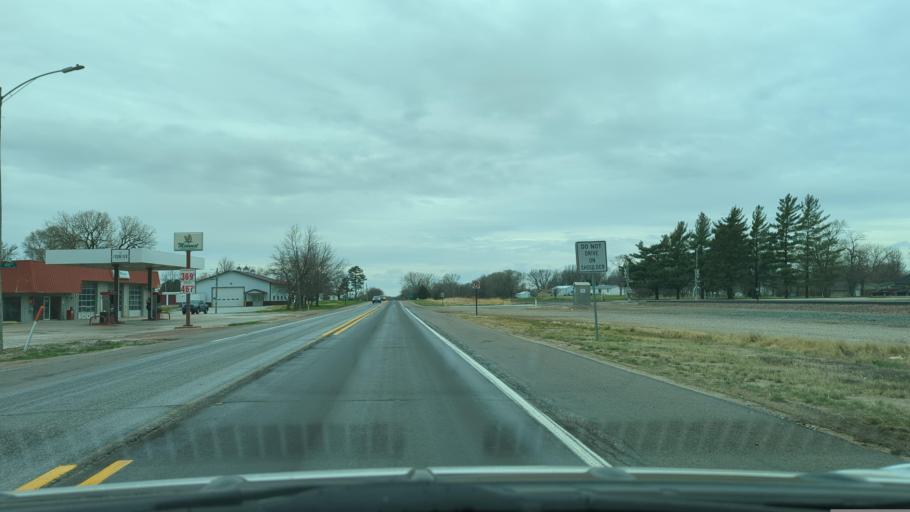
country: US
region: Nebraska
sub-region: Lancaster County
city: Waverly
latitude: 40.9611
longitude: -96.4428
